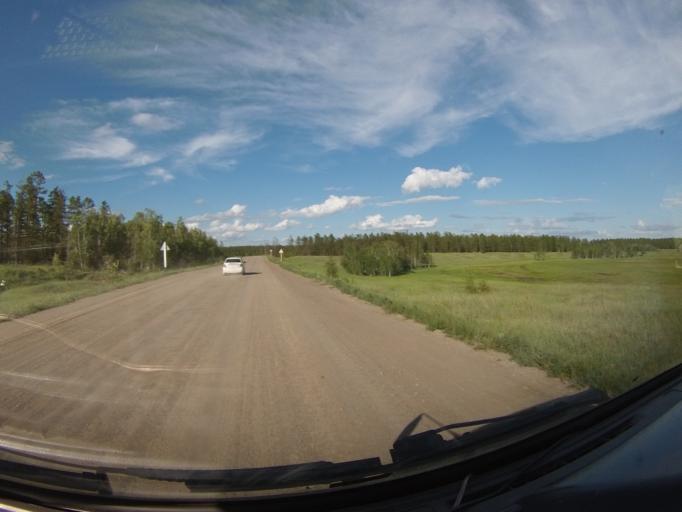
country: RU
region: Sakha
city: Ytyk-Kyuyel'
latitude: 62.2228
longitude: 133.2811
